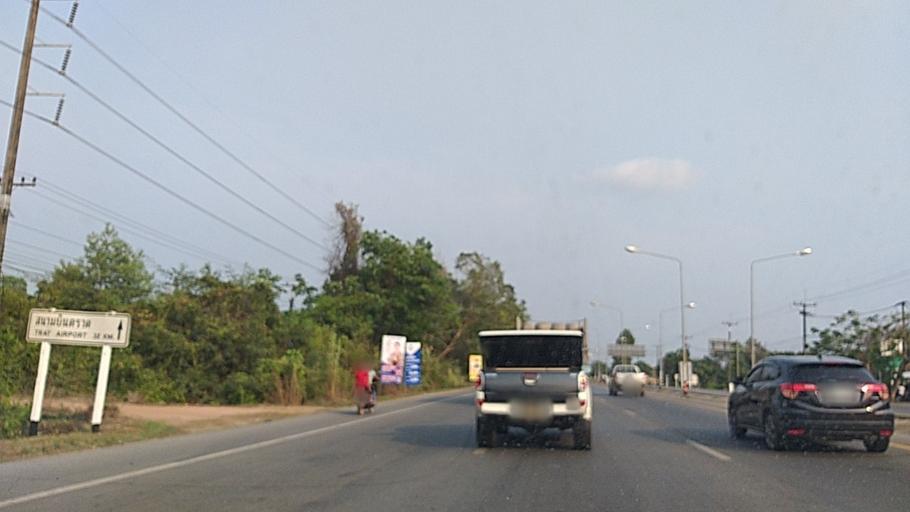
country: TH
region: Chanthaburi
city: Khlung
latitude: 12.4581
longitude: 102.2335
